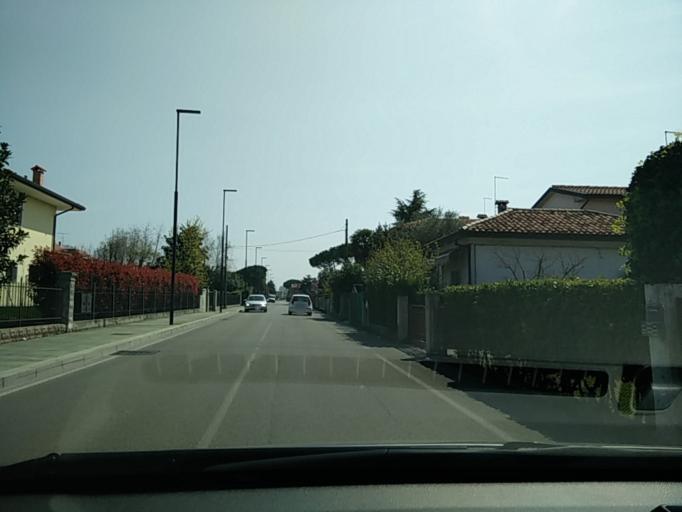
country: IT
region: Veneto
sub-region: Provincia di Venezia
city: San Dona di Piave
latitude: 45.6224
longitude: 12.5661
